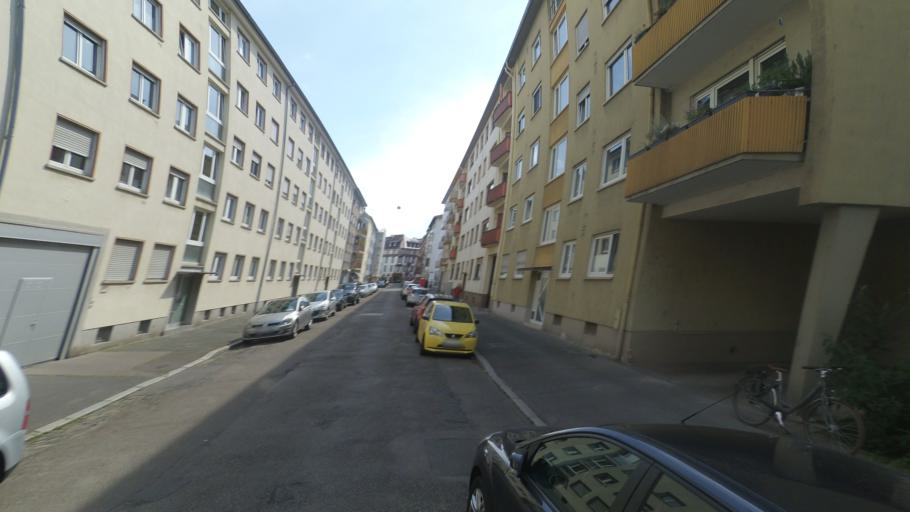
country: DE
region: Rheinland-Pfalz
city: Ludwigshafen am Rhein
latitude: 49.4760
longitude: 8.4665
